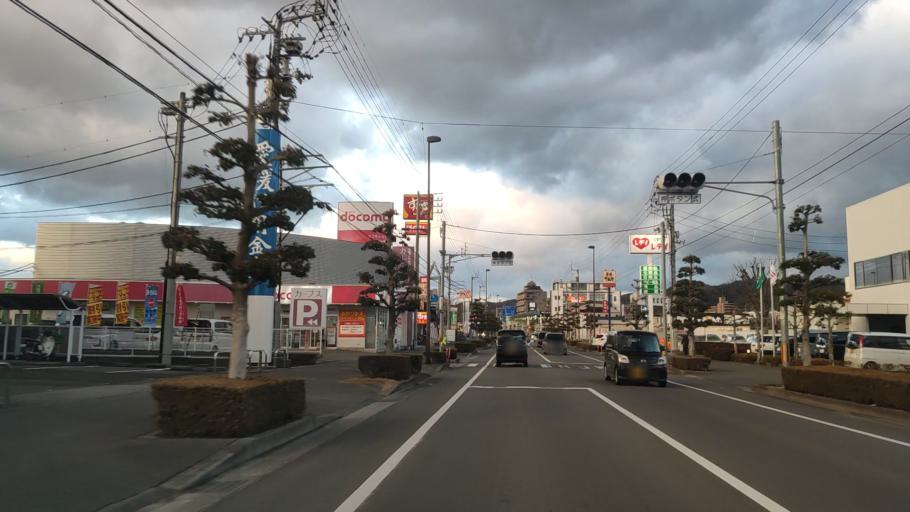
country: JP
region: Ehime
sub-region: Shikoku-chuo Shi
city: Matsuyama
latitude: 33.8355
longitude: 132.7870
